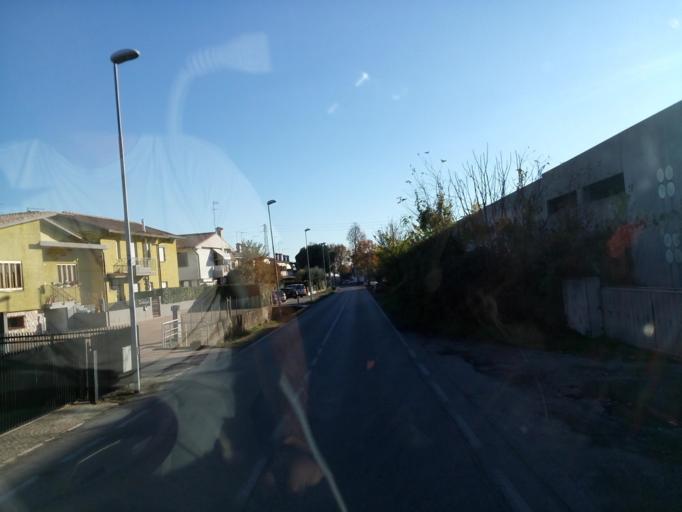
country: IT
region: Veneto
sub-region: Provincia di Treviso
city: Montebelluna
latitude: 45.7786
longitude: 12.0641
